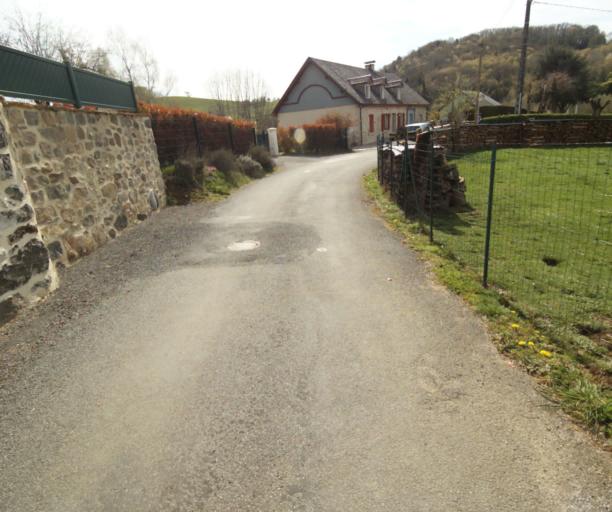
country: FR
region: Limousin
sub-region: Departement de la Correze
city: Laguenne
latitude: 45.2458
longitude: 1.8120
